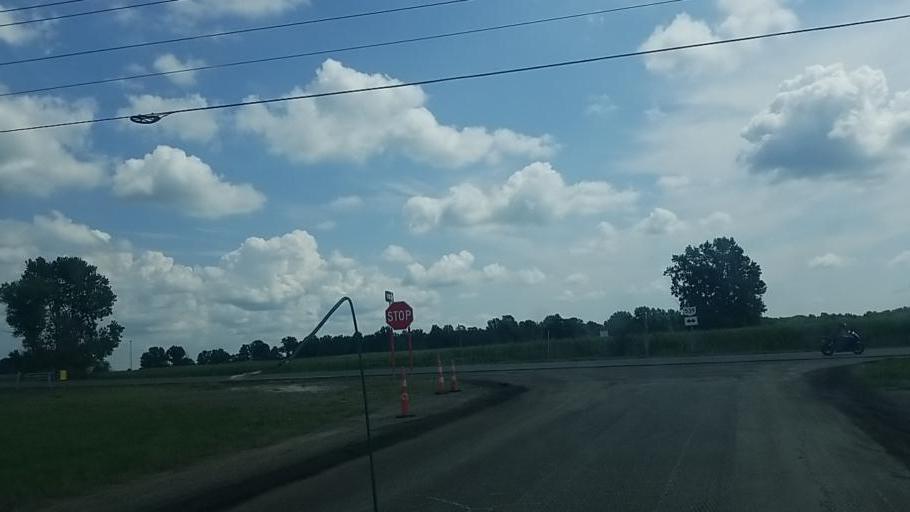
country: US
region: Ohio
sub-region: Wayne County
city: West Salem
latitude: 40.9455
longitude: -82.0826
